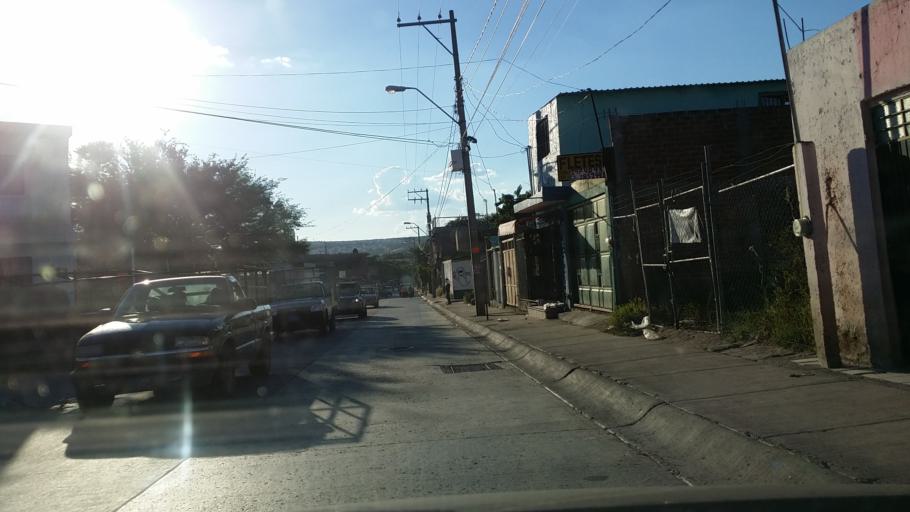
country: MX
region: Guanajuato
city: Leon
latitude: 21.1880
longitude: -101.6776
